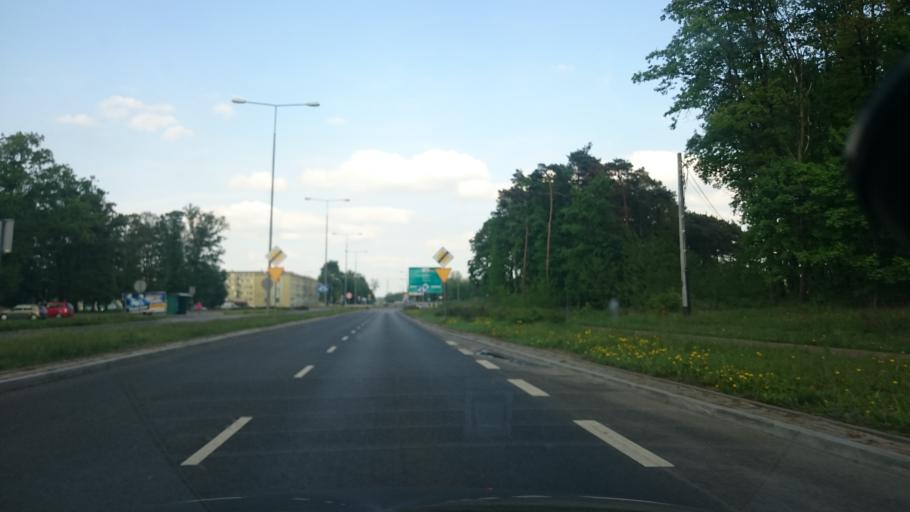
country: PL
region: Kujawsko-Pomorskie
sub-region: Grudziadz
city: Grudziadz
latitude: 53.4712
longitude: 18.7680
